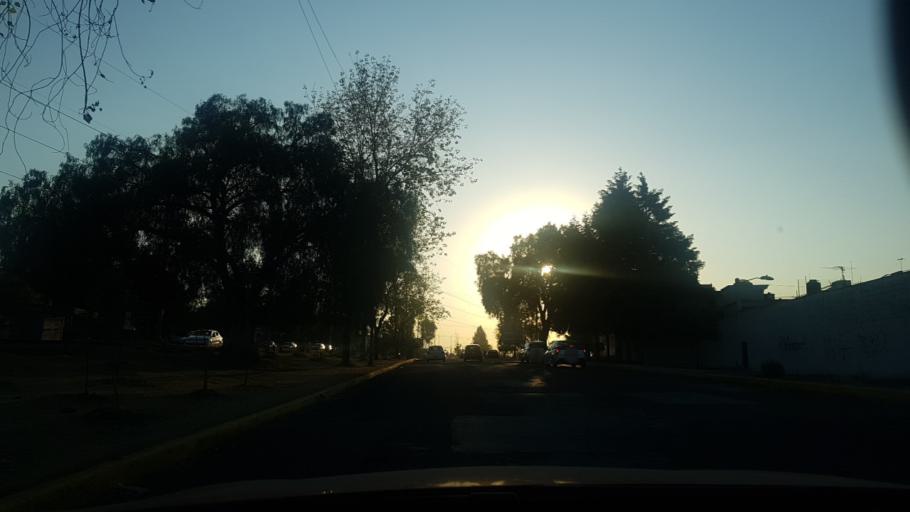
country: MX
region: Mexico
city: Cuautitlan Izcalli
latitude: 19.6376
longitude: -99.2147
